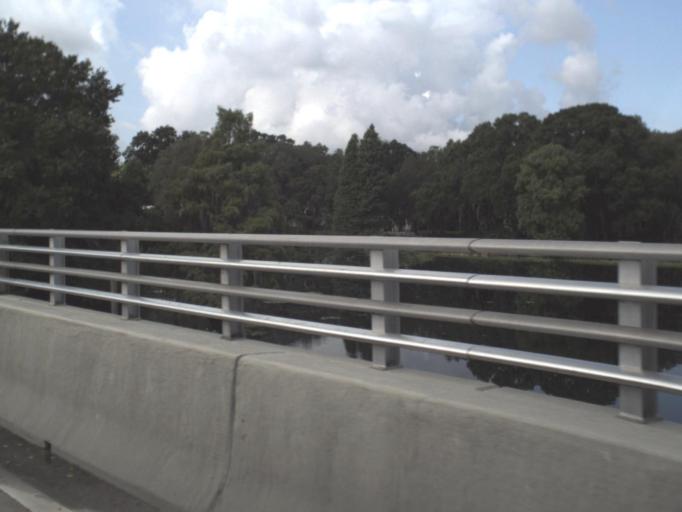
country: US
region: Florida
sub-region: Hillsborough County
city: Temple Terrace
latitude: 28.0244
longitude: -82.3935
